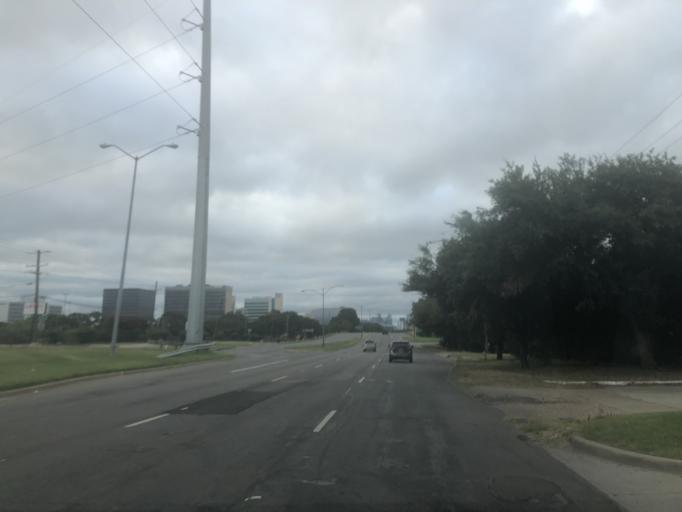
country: US
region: Texas
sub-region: Dallas County
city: University Park
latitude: 32.8244
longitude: -96.8530
